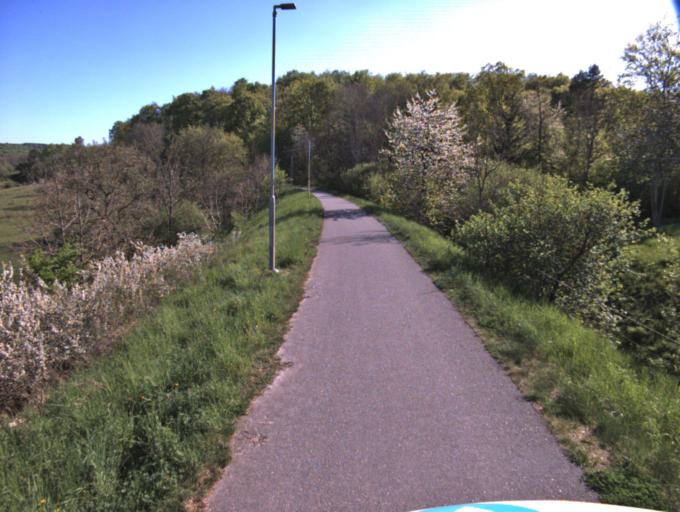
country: SE
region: Skane
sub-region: Kristianstads Kommun
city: Degeberga
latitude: 55.8367
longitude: 14.0787
